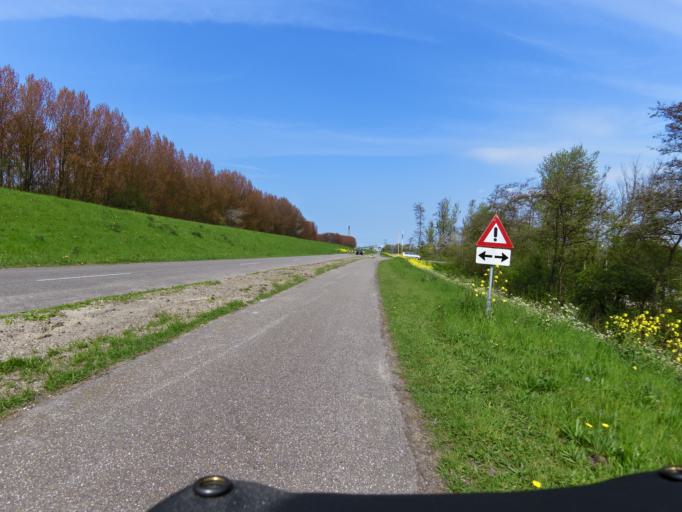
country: NL
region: South Holland
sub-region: Gemeente Rotterdam
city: Hoek van Holland
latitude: 51.9278
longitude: 4.1034
